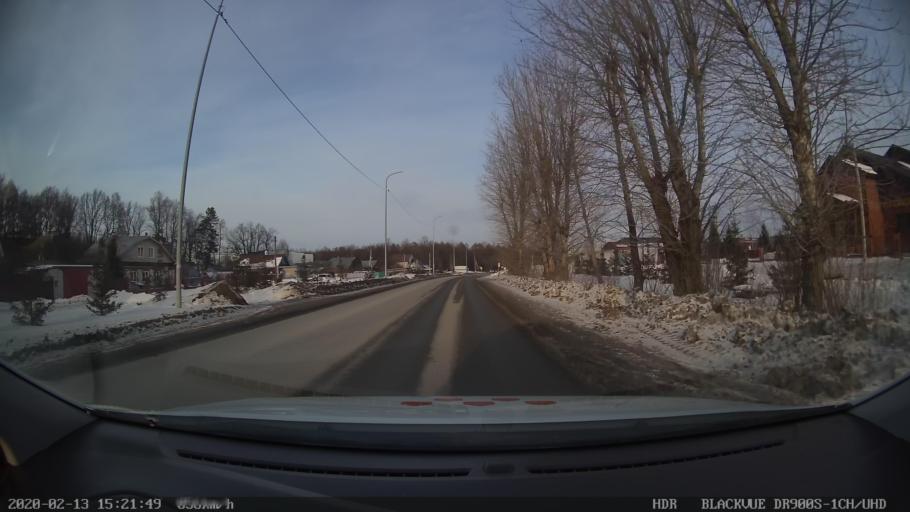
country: RU
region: Tatarstan
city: Vysokaya Gora
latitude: 55.9205
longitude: 49.3035
